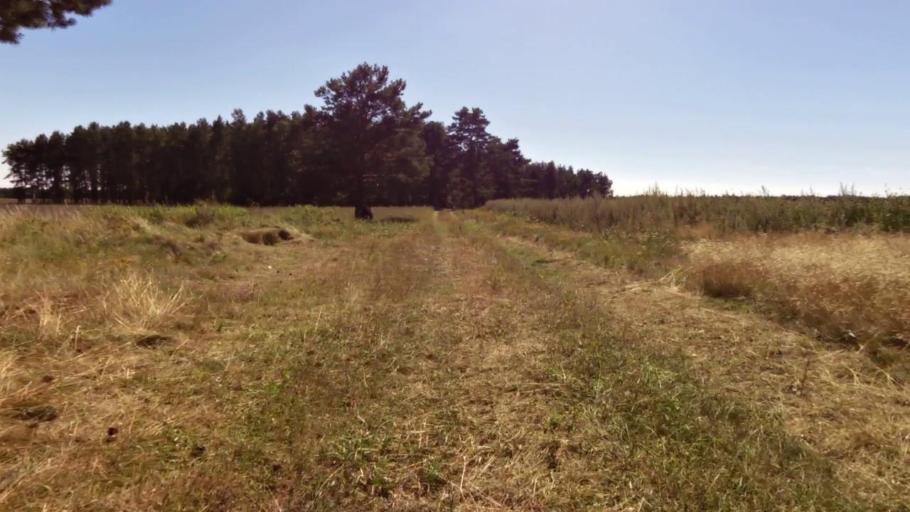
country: PL
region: West Pomeranian Voivodeship
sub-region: Powiat szczecinecki
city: Bialy Bor
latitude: 53.8428
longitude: 16.7464
